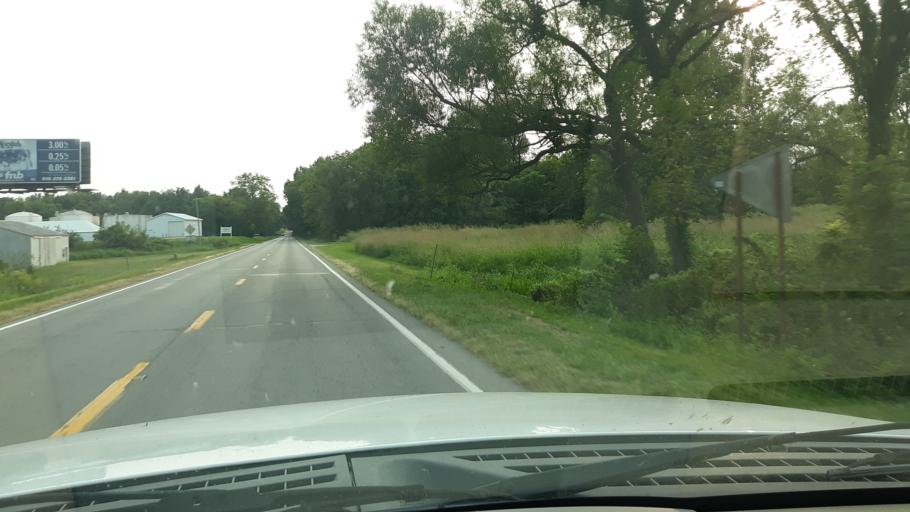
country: US
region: Illinois
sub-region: Wabash County
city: Mount Carmel
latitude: 38.3998
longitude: -87.7959
